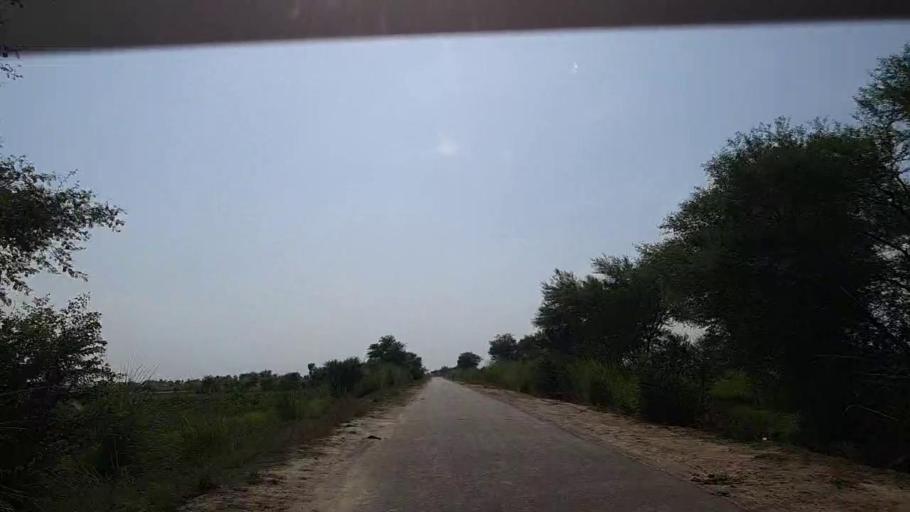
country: PK
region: Sindh
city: Khanpur
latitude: 27.8435
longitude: 69.3910
